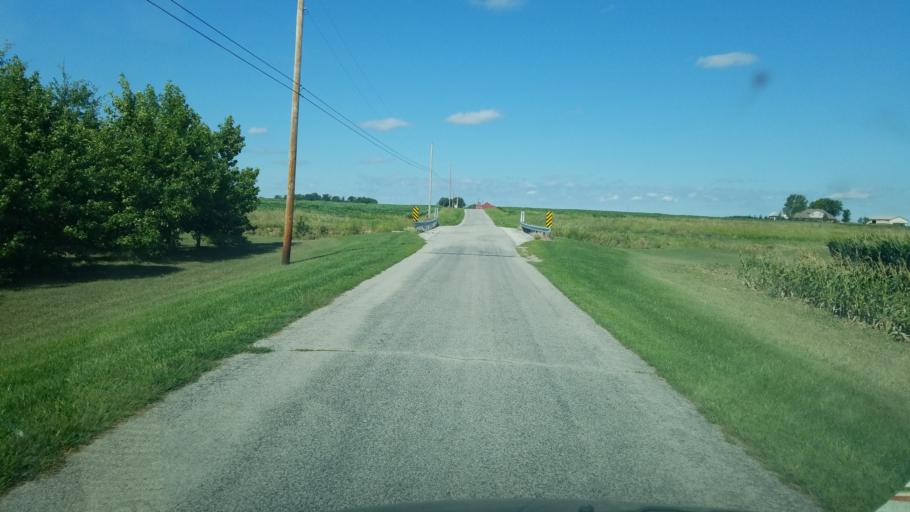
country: US
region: Ohio
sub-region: Hancock County
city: McComb
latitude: 41.1255
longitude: -83.7406
